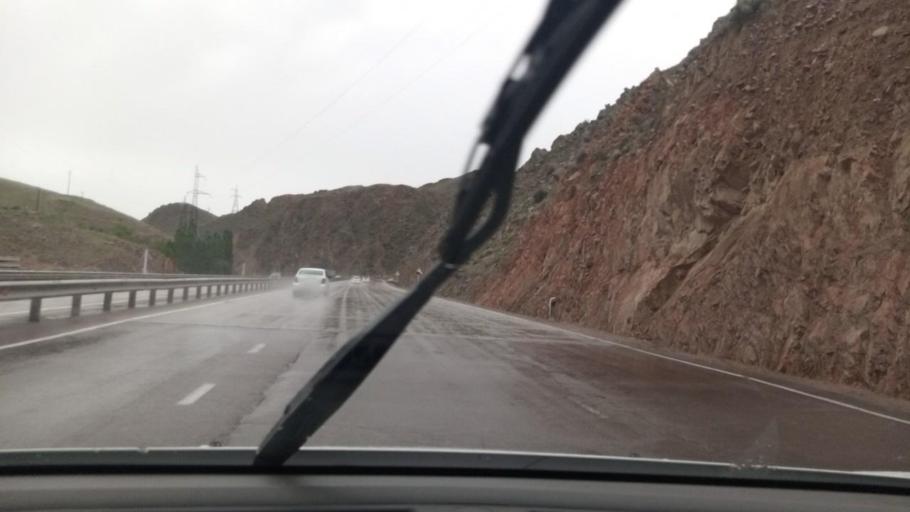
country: TJ
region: Viloyati Sughd
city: Shaydon
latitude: 40.9597
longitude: 70.6661
